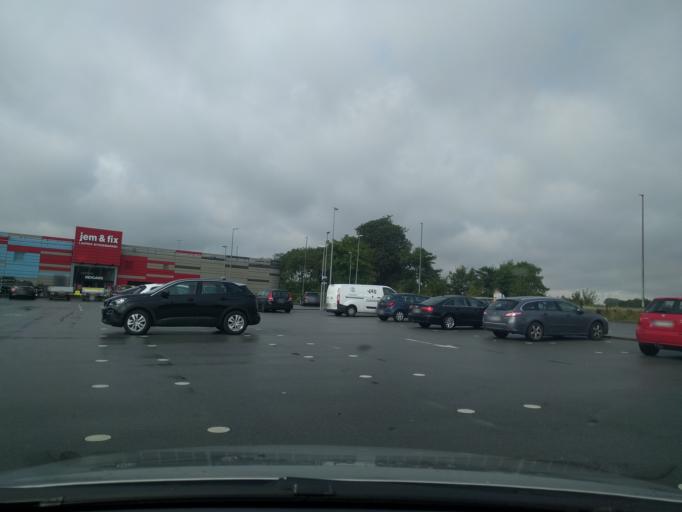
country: DK
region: Zealand
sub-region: Greve Kommune
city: Greve
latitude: 55.5672
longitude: 12.2687
